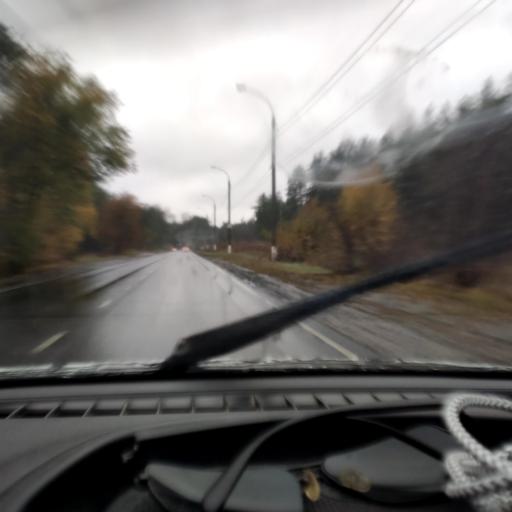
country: RU
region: Samara
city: Zhigulevsk
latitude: 53.4779
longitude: 49.4437
